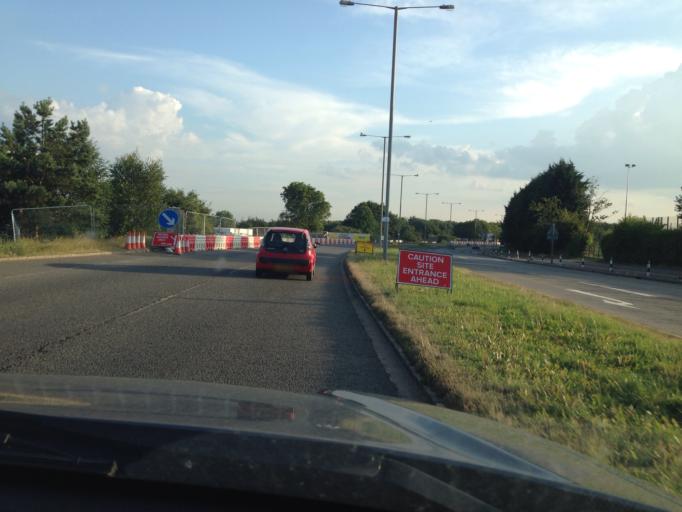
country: GB
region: England
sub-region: Buckinghamshire
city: High Wycombe
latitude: 51.6161
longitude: -0.7629
